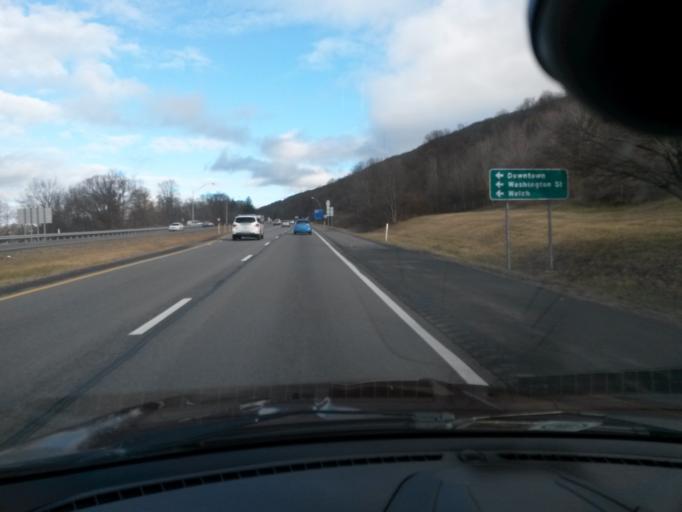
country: US
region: West Virginia
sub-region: Mercer County
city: Bluefield
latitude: 37.2464
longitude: -81.2161
